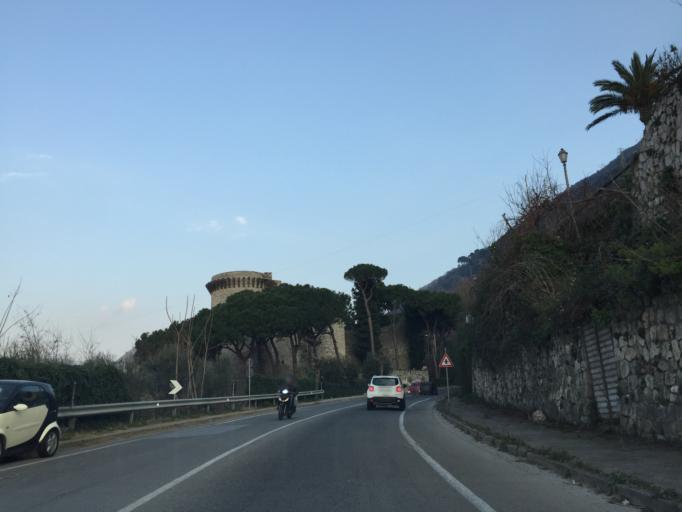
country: IT
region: Campania
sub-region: Provincia di Napoli
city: Castellammare di Stabia
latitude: 40.6888
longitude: 14.4727
